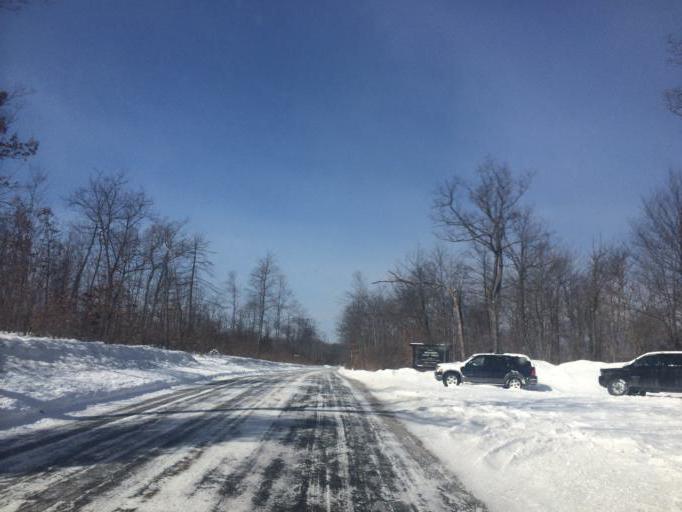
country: US
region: Pennsylvania
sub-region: Centre County
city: Stormstown
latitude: 40.8829
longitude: -78.0215
